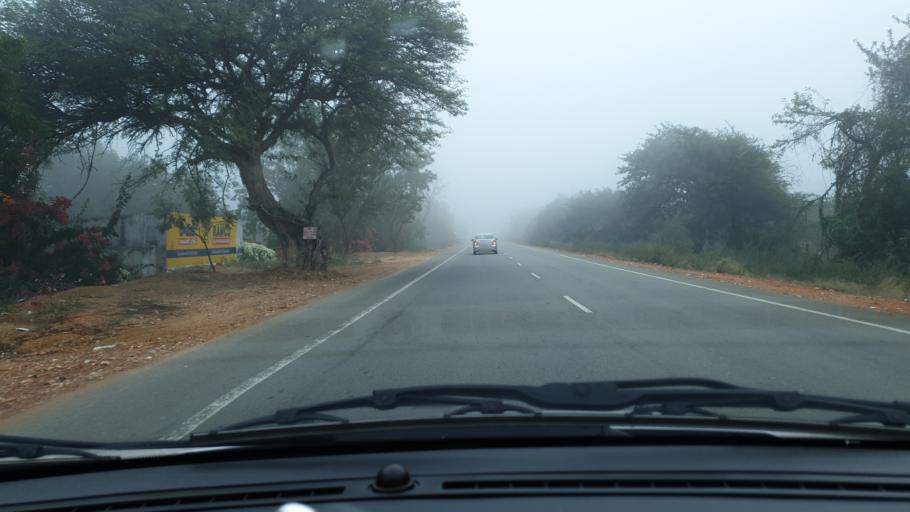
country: IN
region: Telangana
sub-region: Mahbubnagar
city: Nagar Karnul
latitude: 16.6418
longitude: 78.5909
